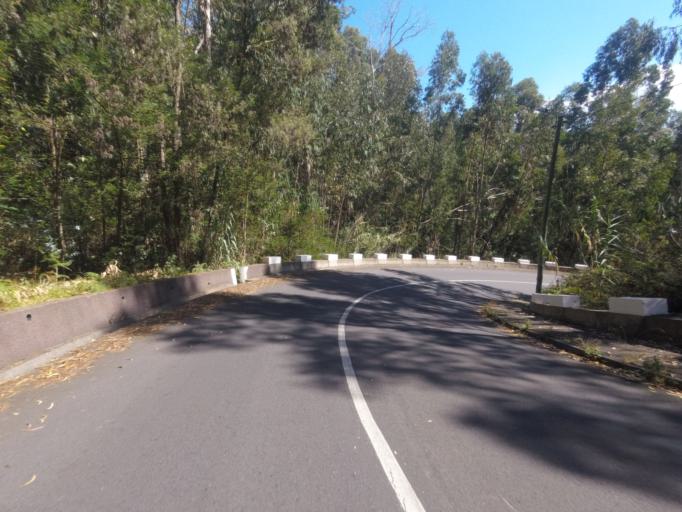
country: PT
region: Madeira
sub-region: Ribeira Brava
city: Campanario
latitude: 32.6868
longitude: -17.0391
